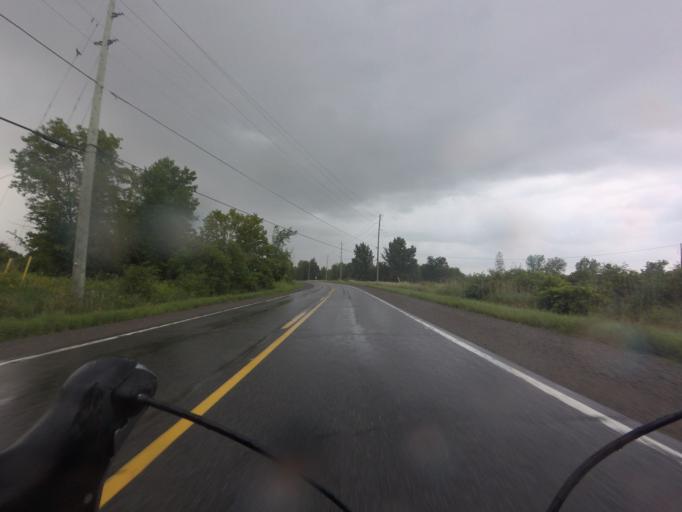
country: CA
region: Ontario
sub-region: Lanark County
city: Smiths Falls
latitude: 44.9463
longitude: -75.8237
